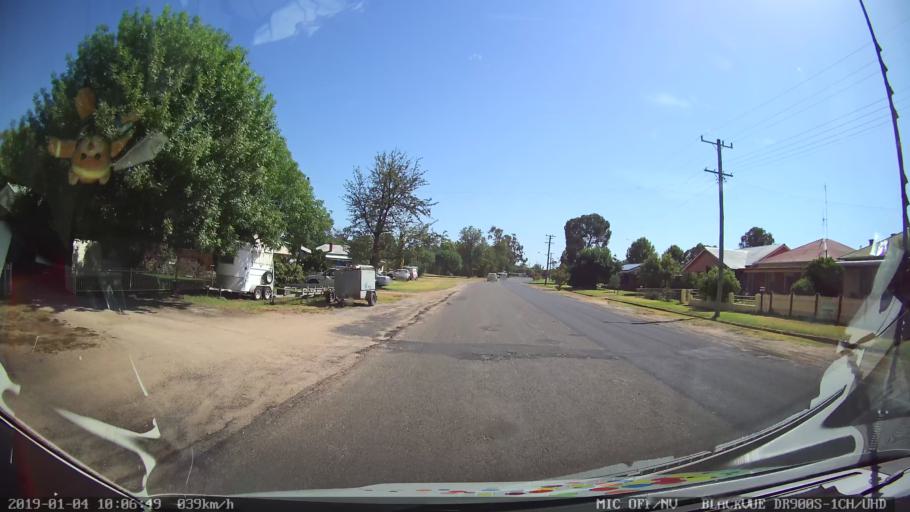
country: AU
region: New South Wales
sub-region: Cabonne
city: Canowindra
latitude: -33.4317
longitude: 148.3700
